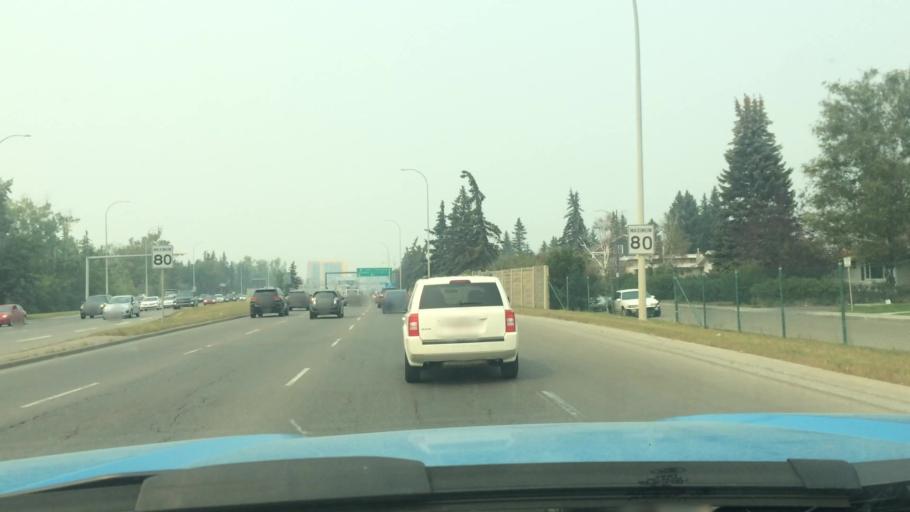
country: CA
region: Alberta
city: Calgary
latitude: 51.0753
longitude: -114.1188
